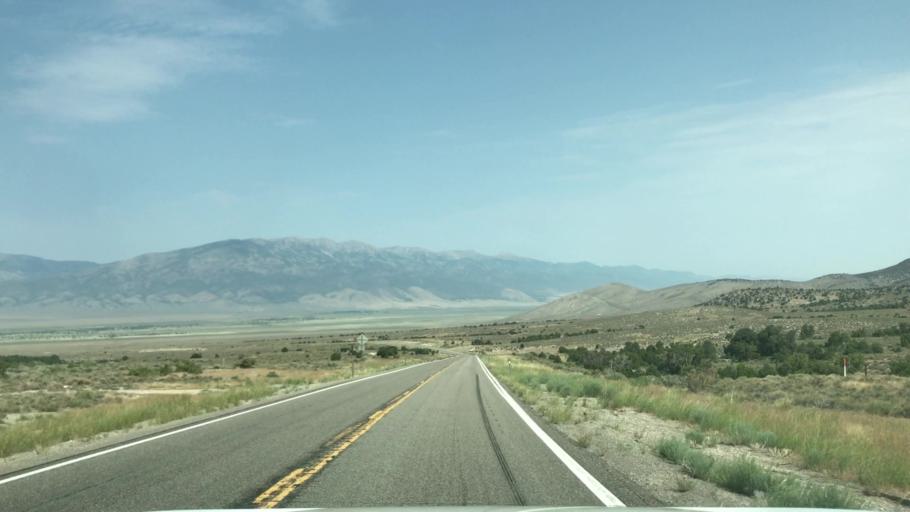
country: US
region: Nevada
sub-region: White Pine County
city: McGill
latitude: 39.1675
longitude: -114.3659
